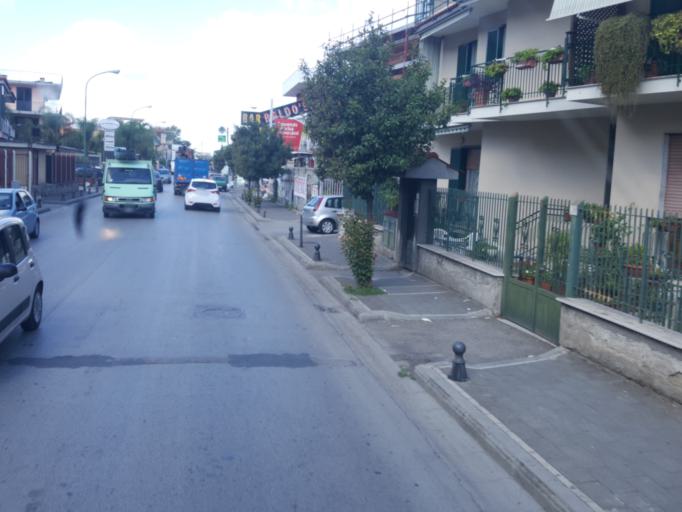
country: IT
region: Campania
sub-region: Provincia di Napoli
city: Nola
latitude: 40.9168
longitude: 14.5238
